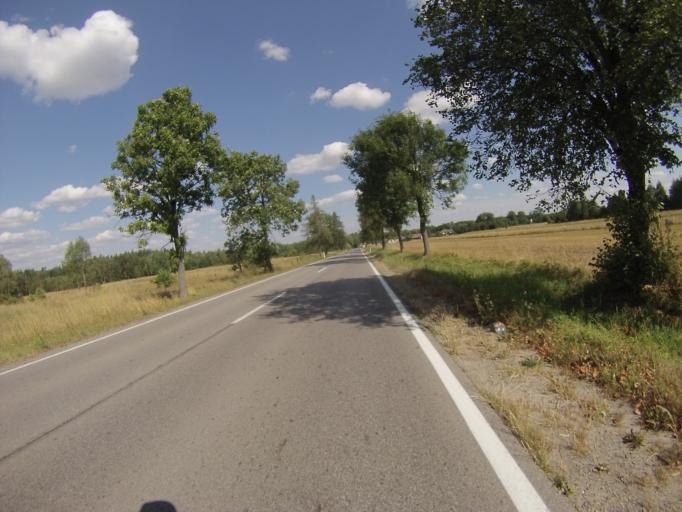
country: PL
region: Swietokrzyskie
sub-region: Powiat kielecki
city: Rakow
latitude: 50.6935
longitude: 21.0597
